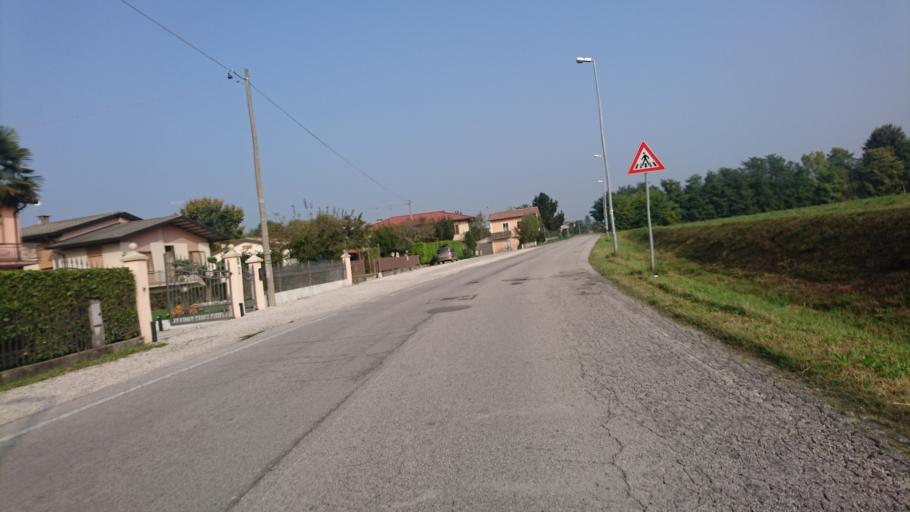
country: IT
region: Veneto
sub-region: Provincia di Padova
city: Pieve
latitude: 45.5399
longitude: 11.8333
